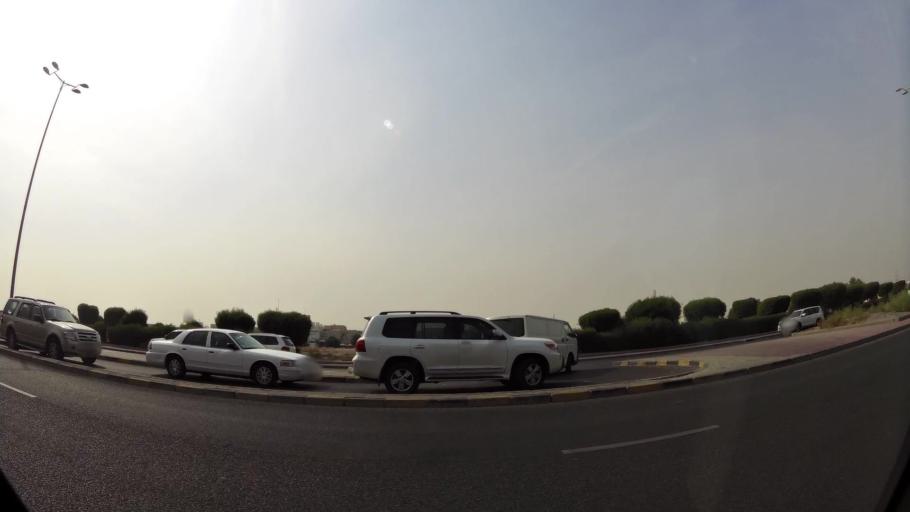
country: KW
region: Al Asimah
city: Ar Rabiyah
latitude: 29.2918
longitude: 47.9284
